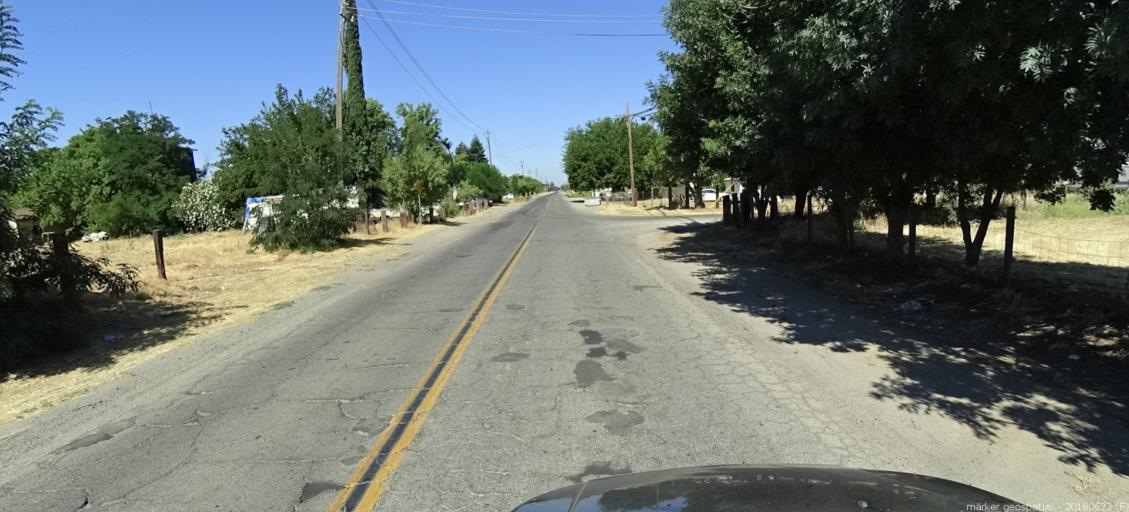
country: US
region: California
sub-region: Madera County
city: Parksdale
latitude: 36.9744
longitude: -120.0260
